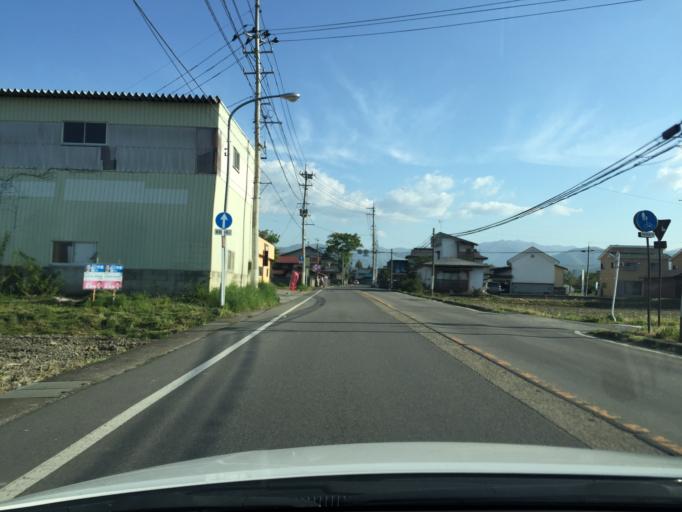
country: JP
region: Fukushima
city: Kitakata
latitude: 37.6677
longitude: 139.8716
